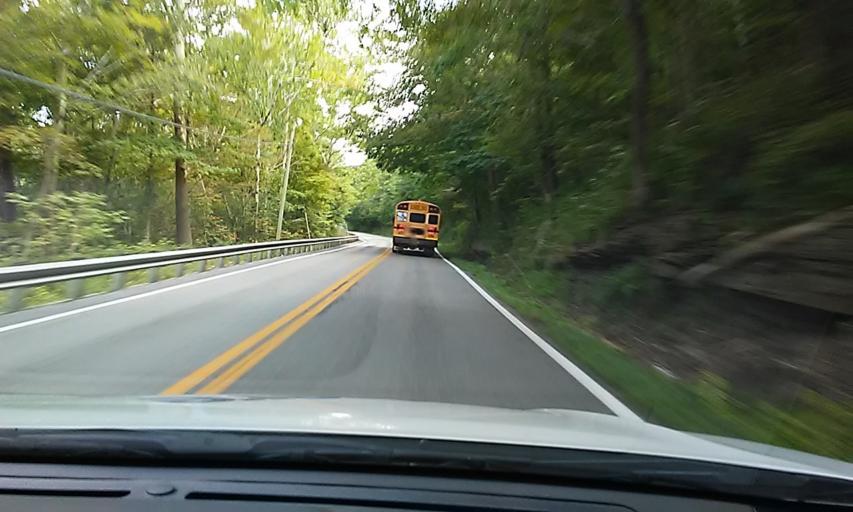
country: US
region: West Virginia
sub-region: Monongalia County
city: Star City
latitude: 39.7095
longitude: -80.1249
